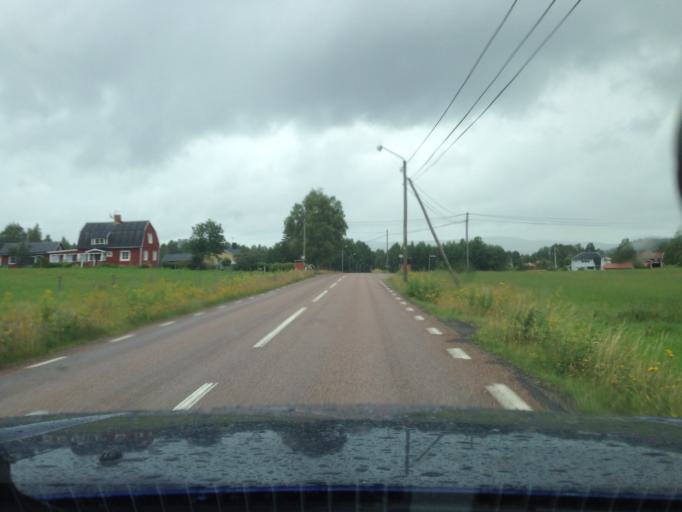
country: SE
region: Dalarna
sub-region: Ludvika Kommun
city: Grangesberg
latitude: 60.1406
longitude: 14.9968
